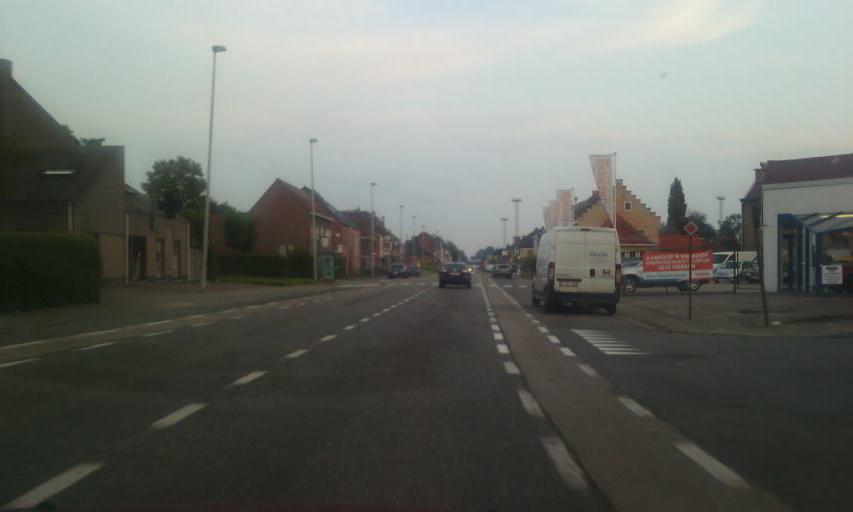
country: BE
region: Flanders
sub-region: Provincie Oost-Vlaanderen
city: Dendermonde
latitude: 51.0471
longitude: 4.1078
